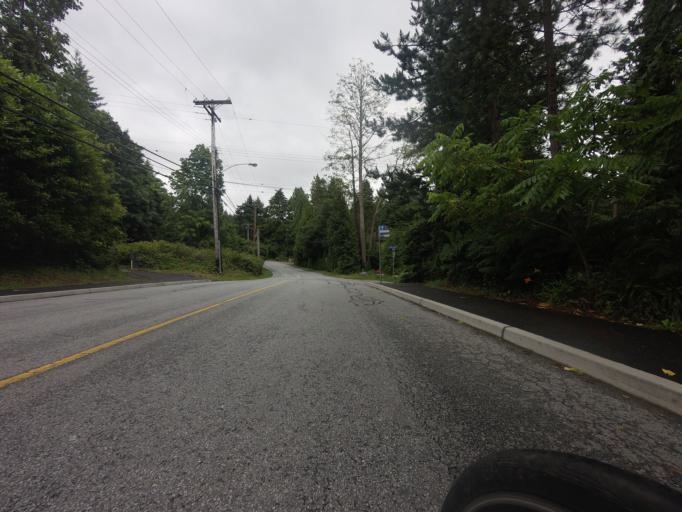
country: CA
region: British Columbia
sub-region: Greater Vancouver Regional District
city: Bowen Island
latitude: 49.3421
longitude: -123.2653
